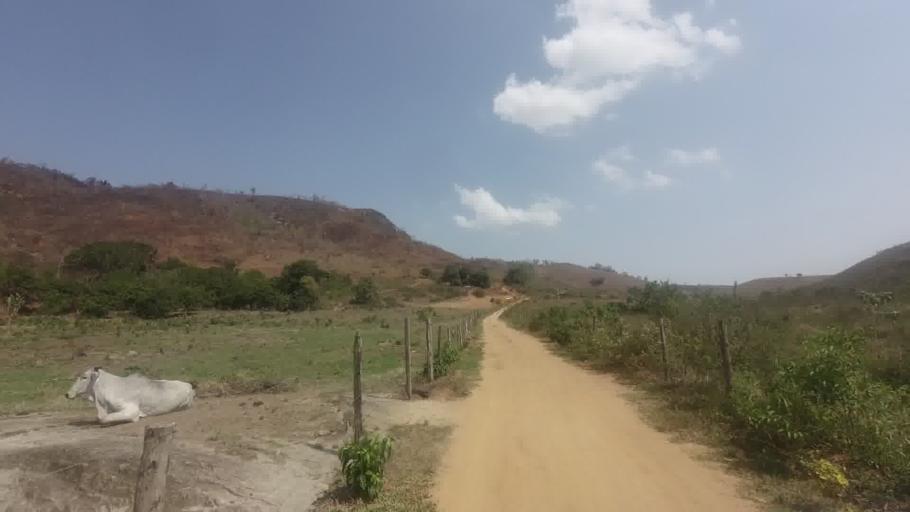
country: BR
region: Espirito Santo
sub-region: Sao Jose Do Calcado
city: Sao Jose do Calcado
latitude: -21.0282
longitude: -41.5169
